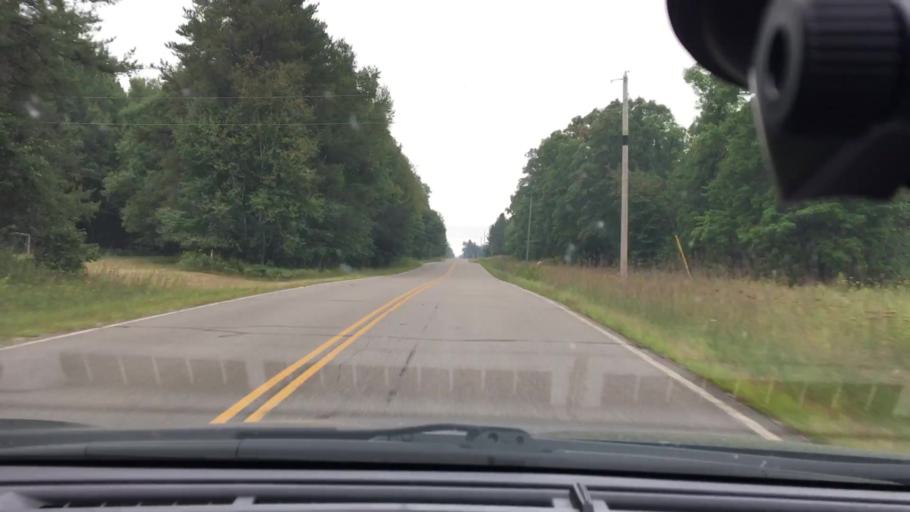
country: US
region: Minnesota
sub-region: Crow Wing County
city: Cross Lake
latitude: 46.6516
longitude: -94.0094
